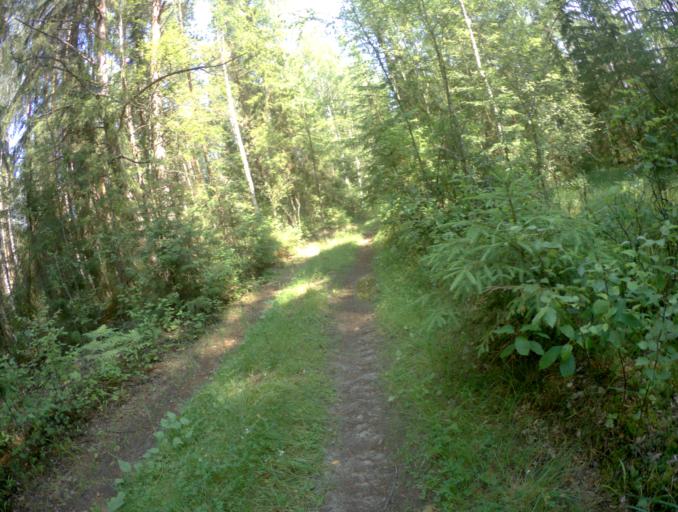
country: RU
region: Vladimir
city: Vyazniki
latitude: 56.3533
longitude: 42.2337
